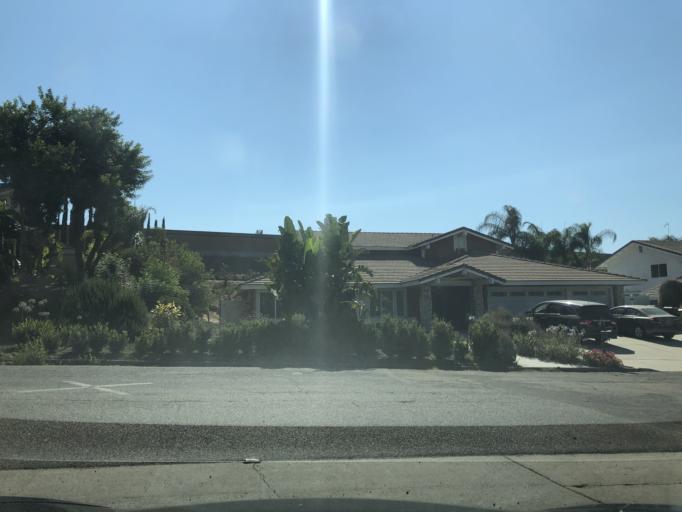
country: US
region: California
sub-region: Riverside County
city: El Cerrito
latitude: 33.8590
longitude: -117.5348
